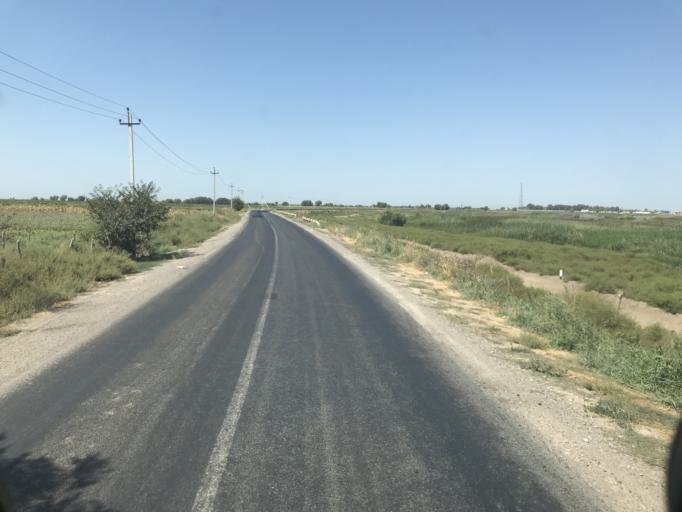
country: KZ
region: Ongtustik Qazaqstan
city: Ilyich
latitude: 40.9509
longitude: 68.4802
